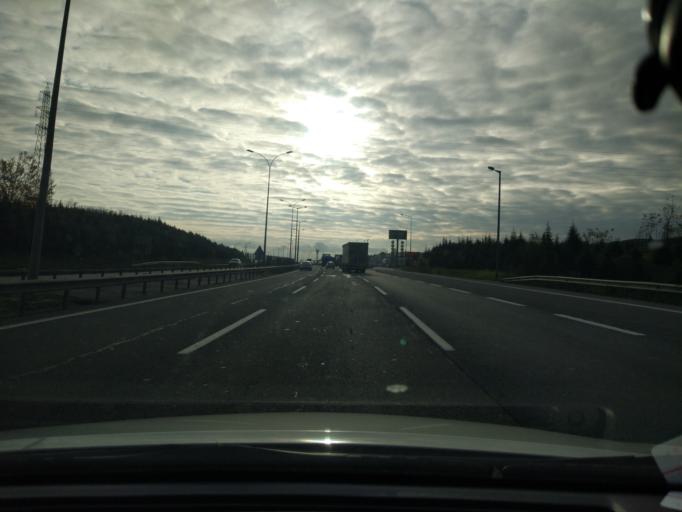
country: TR
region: Kocaeli
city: Balcik
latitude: 40.8380
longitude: 29.4176
